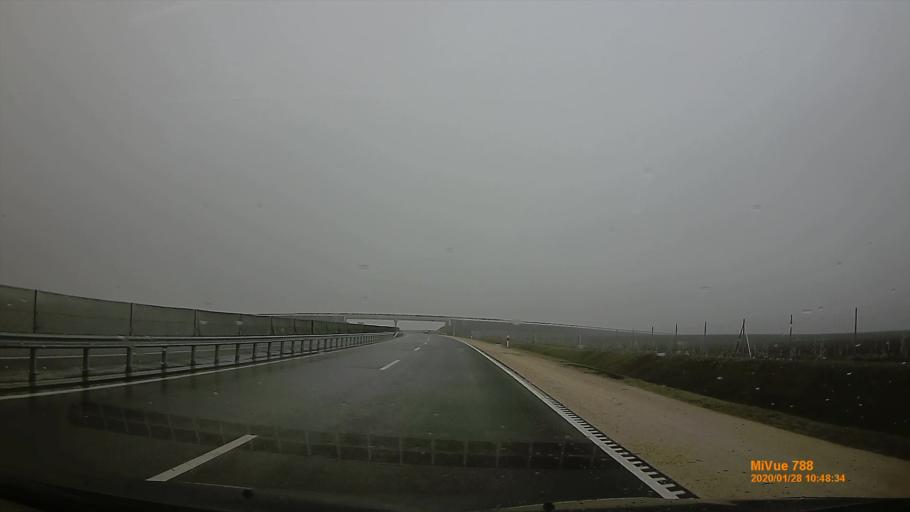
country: HU
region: Pest
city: Monor
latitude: 47.3811
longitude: 19.4627
